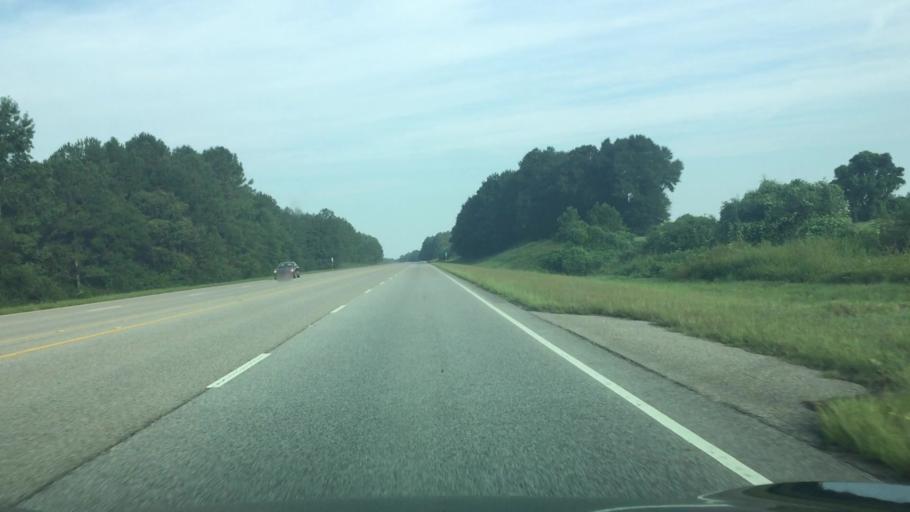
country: US
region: Alabama
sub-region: Covington County
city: Andalusia
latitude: 31.4000
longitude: -86.5828
